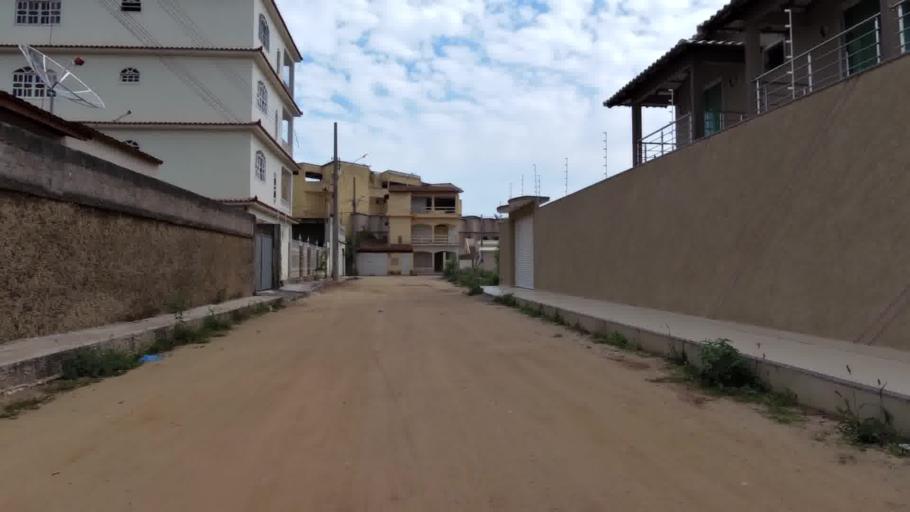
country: BR
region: Espirito Santo
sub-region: Piuma
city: Piuma
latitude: -20.8414
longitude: -40.7350
